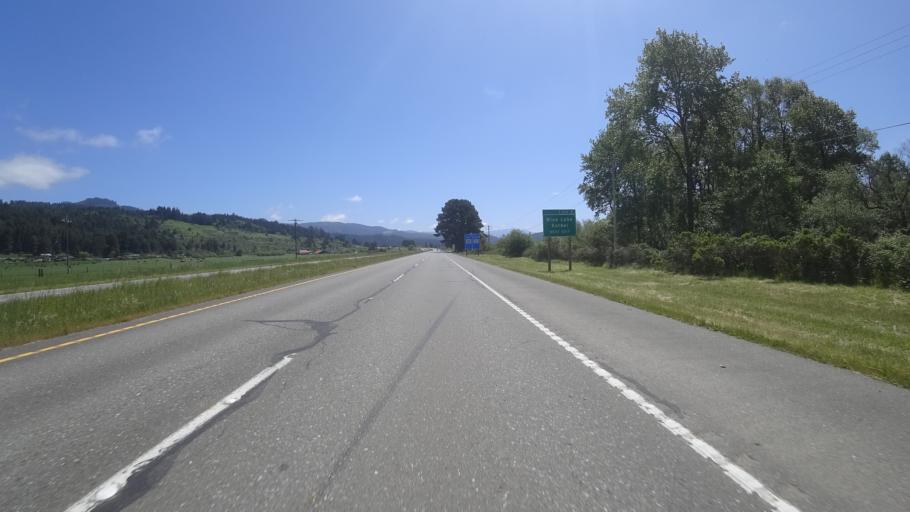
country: US
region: California
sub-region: Humboldt County
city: Blue Lake
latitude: 40.8929
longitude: -124.0110
